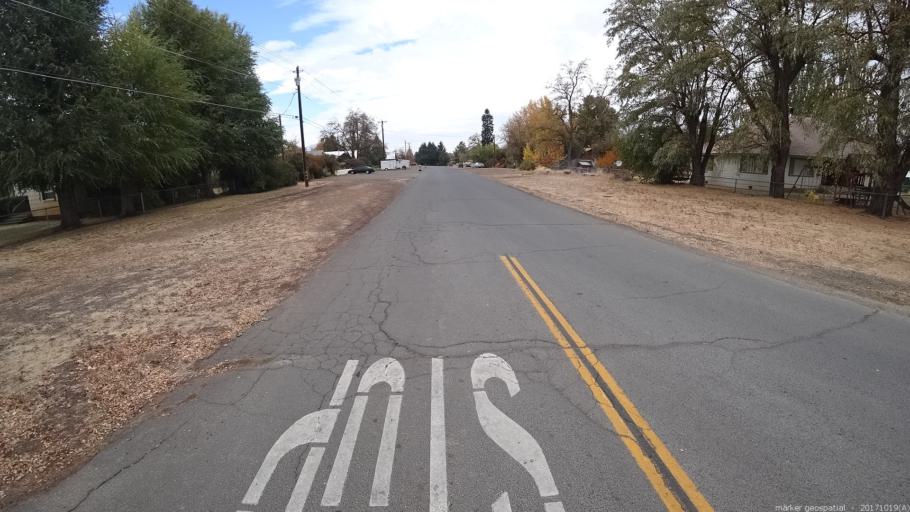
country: US
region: California
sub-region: Shasta County
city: Burney
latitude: 41.0482
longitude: -121.4008
